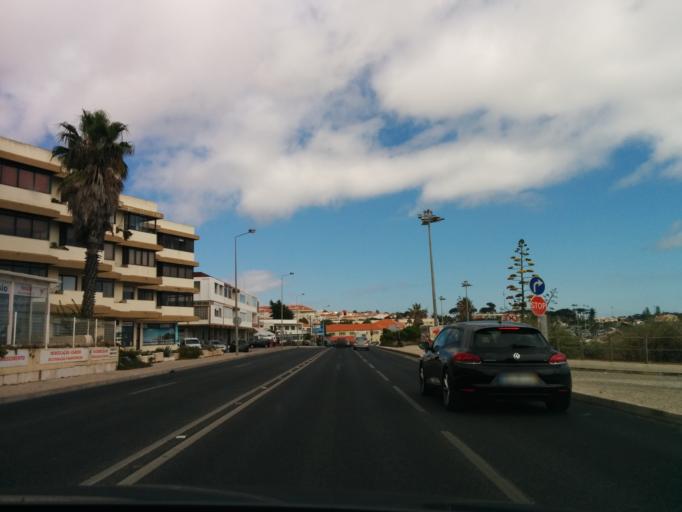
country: PT
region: Lisbon
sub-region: Cascais
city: Parede
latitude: 38.6941
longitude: -9.3717
